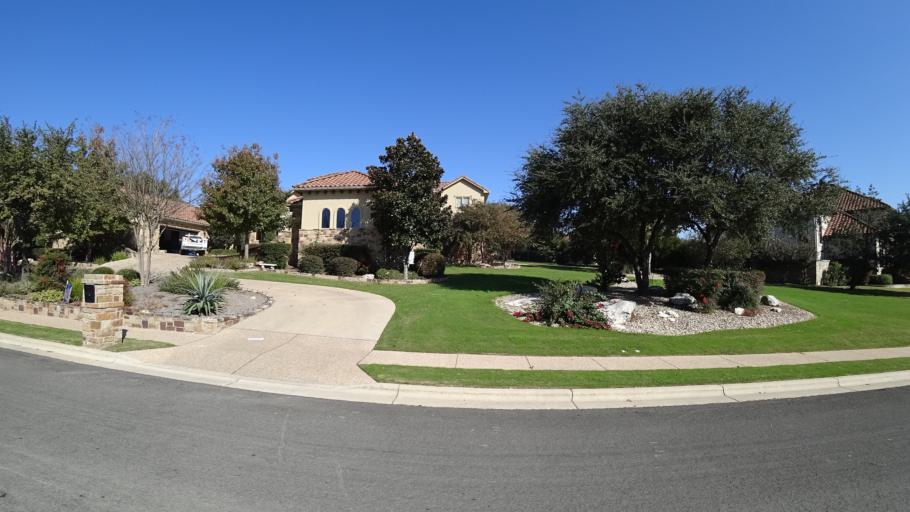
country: US
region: Texas
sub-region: Williamson County
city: Anderson Mill
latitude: 30.3848
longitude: -97.8468
